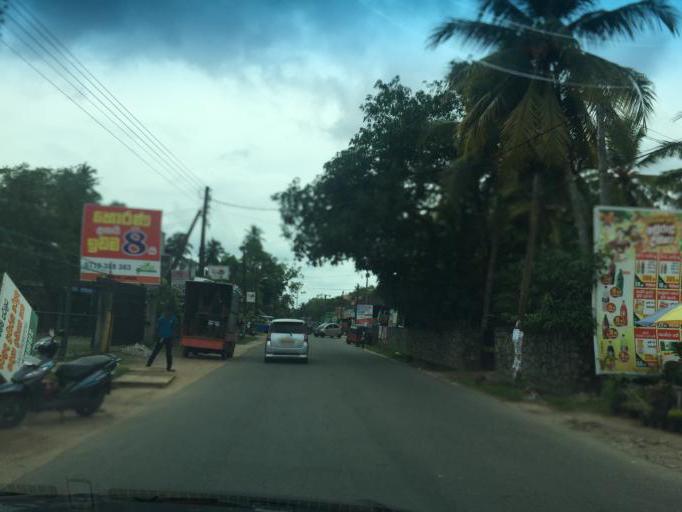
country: LK
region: Western
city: Horana South
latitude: 6.7099
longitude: 80.0661
